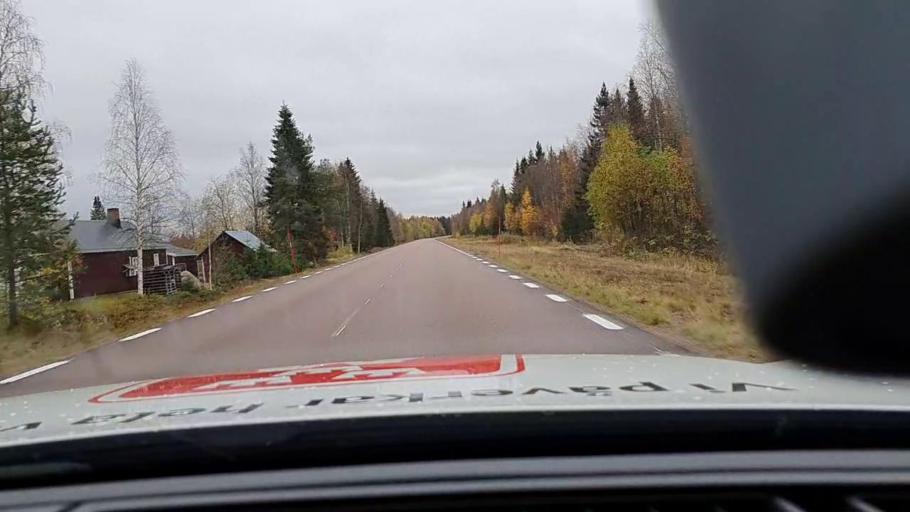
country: FI
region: Lapland
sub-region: Kemi-Tornio
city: Tornio
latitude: 66.0535
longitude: 23.9376
